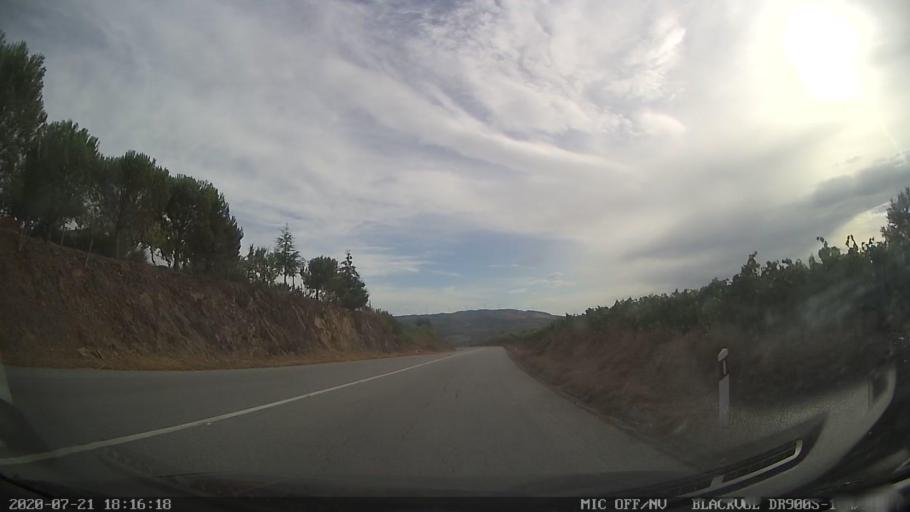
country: PT
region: Viseu
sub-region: Sao Joao da Pesqueira
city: Sao Joao da Pesqueira
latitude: 41.1102
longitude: -7.3876
